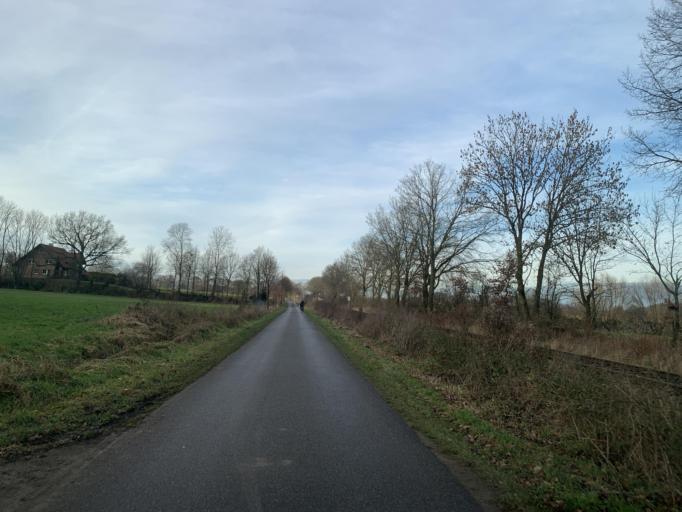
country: DE
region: North Rhine-Westphalia
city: Ludinghausen
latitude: 51.7903
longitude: 7.3874
